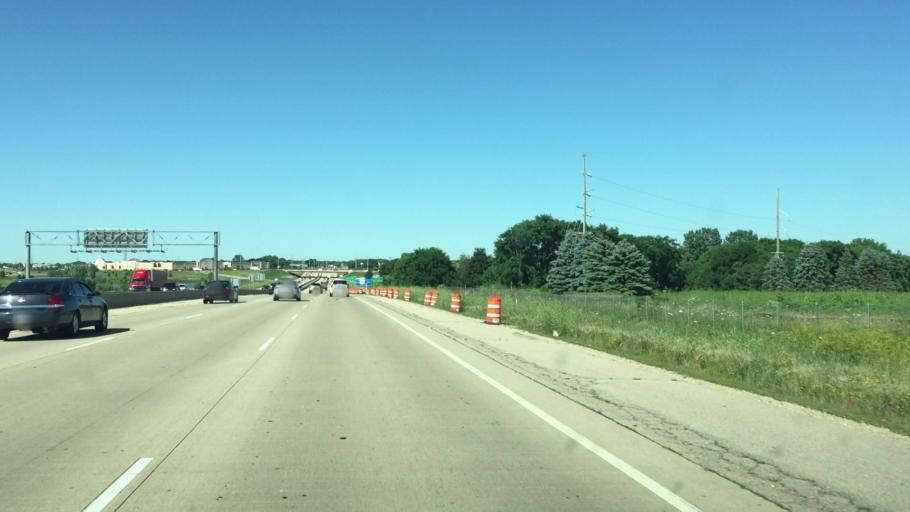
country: US
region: Wisconsin
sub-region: Dane County
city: Sun Prairie
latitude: 43.1544
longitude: -89.2749
